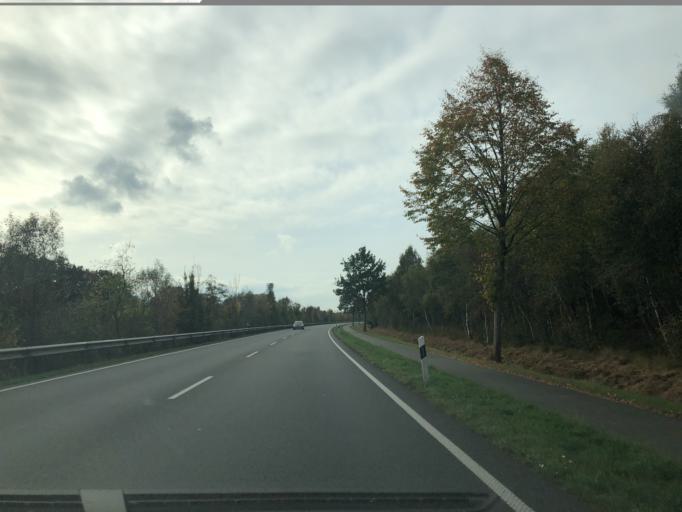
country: DE
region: Lower Saxony
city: Friesoythe
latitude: 53.0374
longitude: 7.7862
